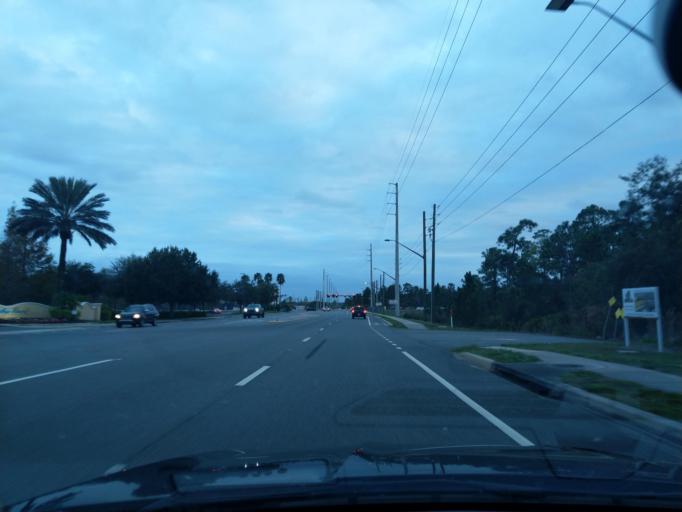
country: US
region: Florida
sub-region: Orange County
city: Williamsburg
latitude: 28.3881
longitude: -81.4831
